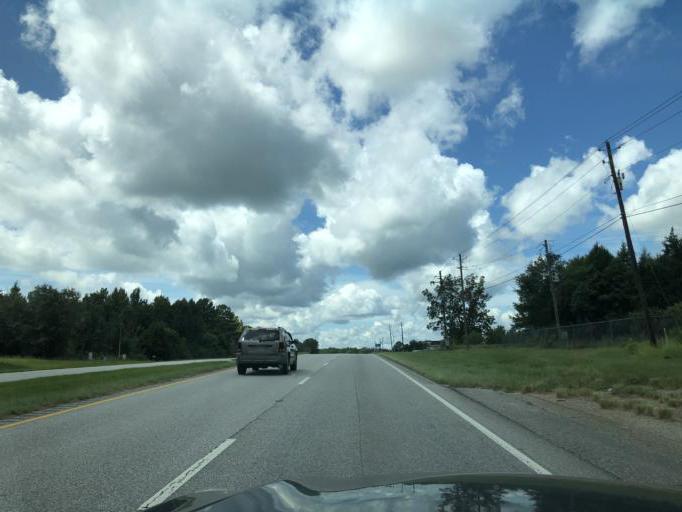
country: US
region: Alabama
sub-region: Barbour County
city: Eufaula
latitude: 31.9415
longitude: -85.1305
